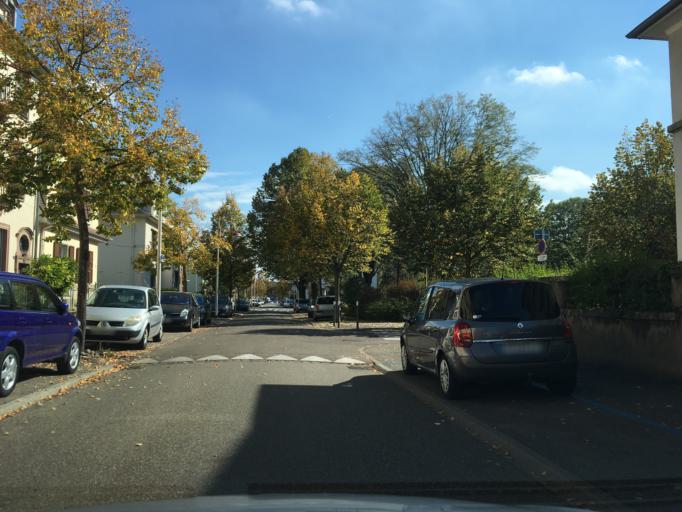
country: FR
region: Alsace
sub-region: Departement du Haut-Rhin
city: Colmar
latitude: 48.0735
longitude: 7.3420
